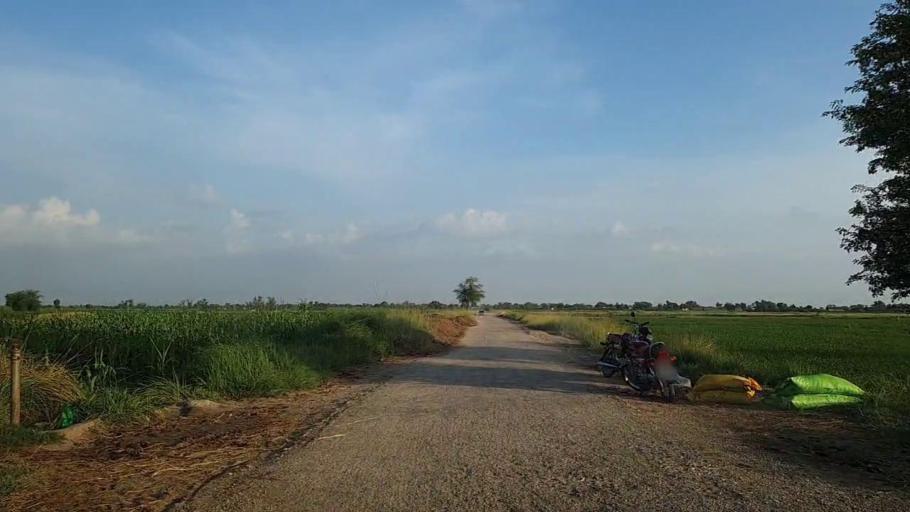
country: PK
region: Sindh
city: Karaundi
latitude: 27.0521
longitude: 68.4043
